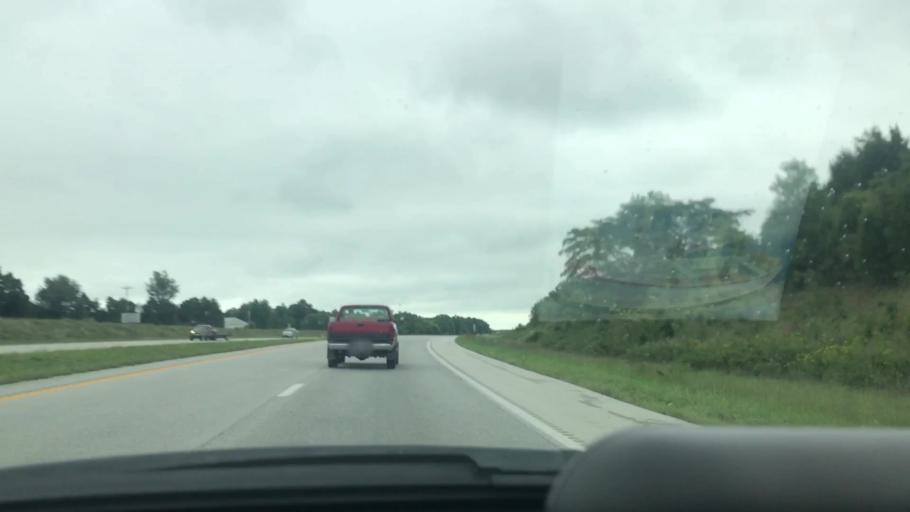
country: US
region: Missouri
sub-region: Greene County
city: Strafford
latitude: 37.2809
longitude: -93.2035
